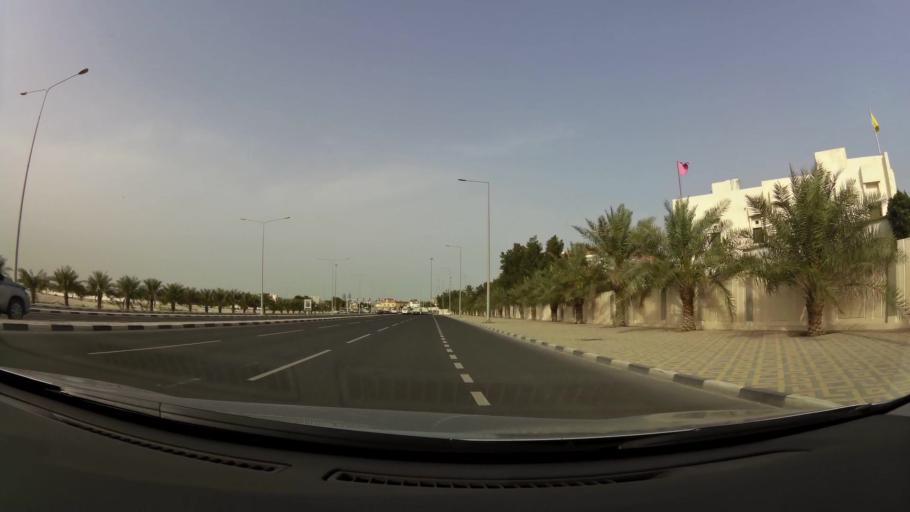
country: QA
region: Baladiyat ad Dawhah
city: Doha
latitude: 25.3268
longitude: 51.5037
